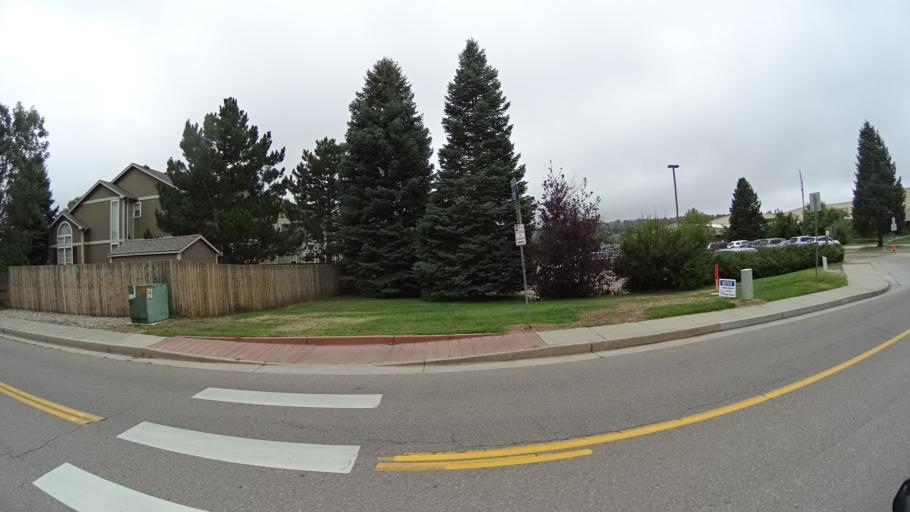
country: US
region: Colorado
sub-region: El Paso County
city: Cimarron Hills
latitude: 38.9323
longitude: -104.7567
